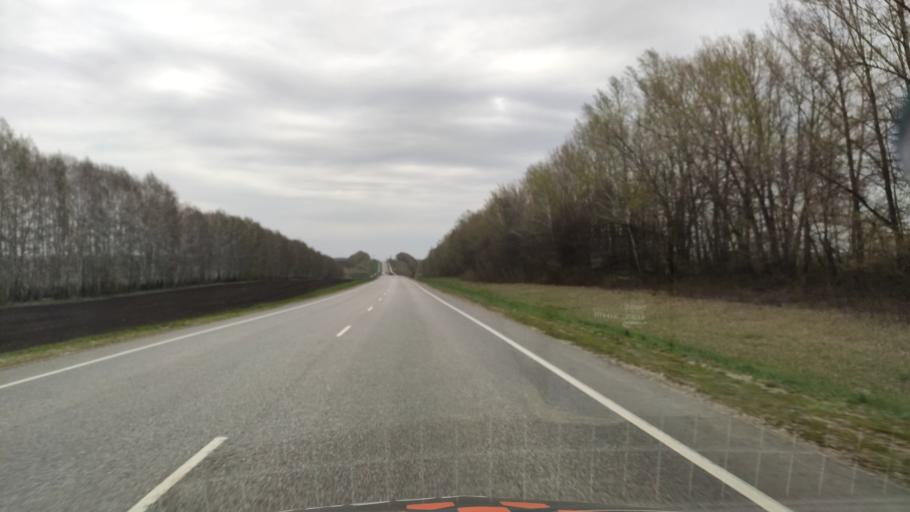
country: RU
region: Kursk
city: Olym
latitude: 51.5539
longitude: 38.2229
